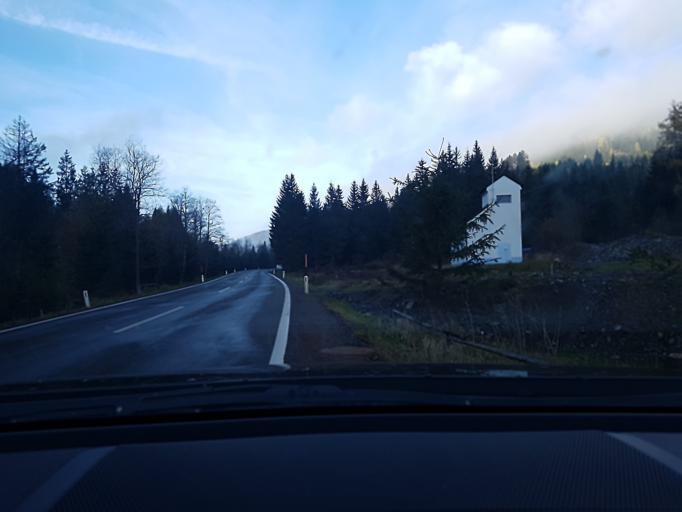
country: AT
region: Styria
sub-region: Politischer Bezirk Murtal
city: Pusterwald
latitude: 47.2329
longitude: 14.3744
